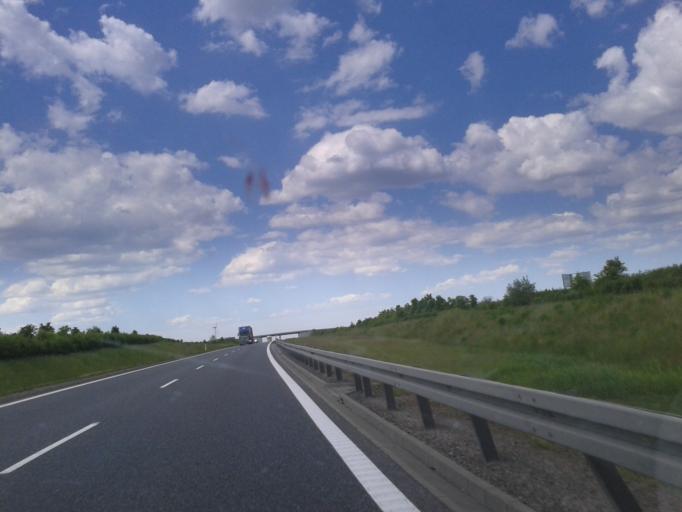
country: PL
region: Pomeranian Voivodeship
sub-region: Powiat chojnicki
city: Chojnice
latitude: 53.6804
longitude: 17.5512
